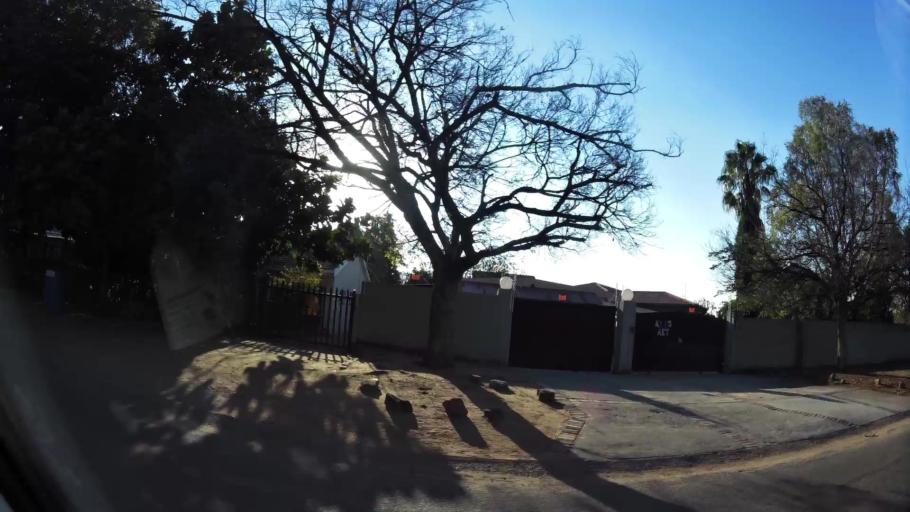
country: ZA
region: North-West
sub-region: Bojanala Platinum District Municipality
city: Rustenburg
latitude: -25.6808
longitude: 27.2267
